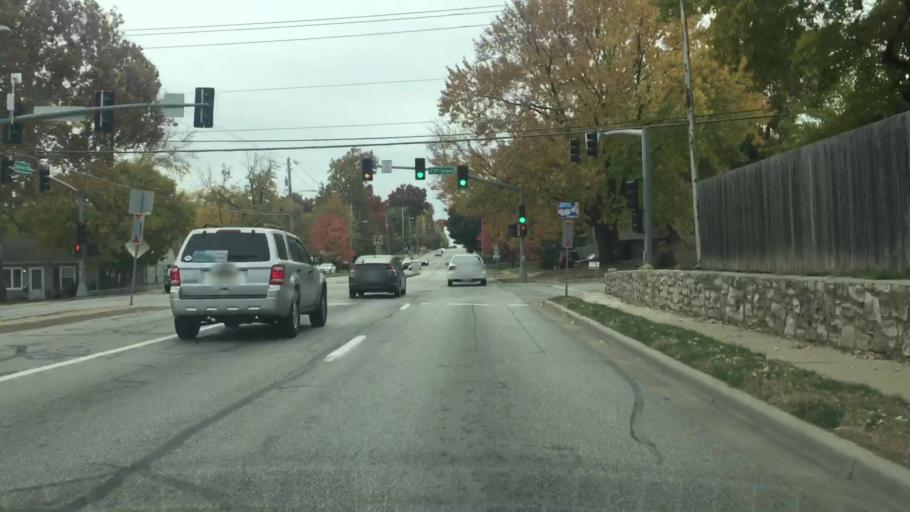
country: US
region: Kansas
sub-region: Johnson County
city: Shawnee
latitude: 39.0077
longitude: -94.7239
